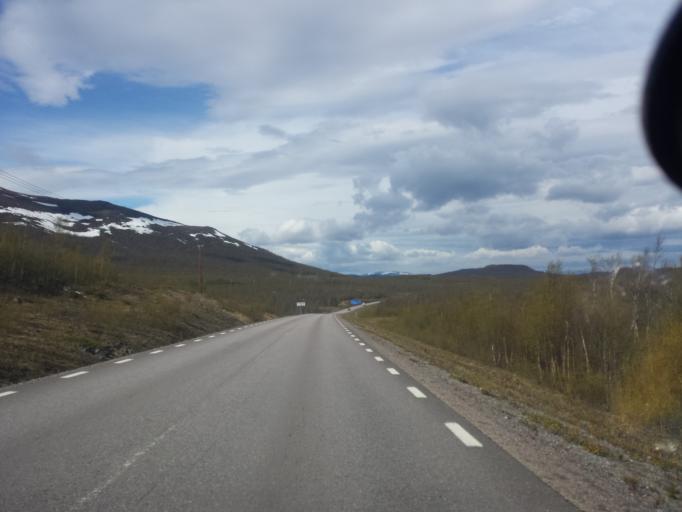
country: SE
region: Norrbotten
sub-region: Kiruna Kommun
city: Kiruna
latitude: 68.1584
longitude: 19.7776
